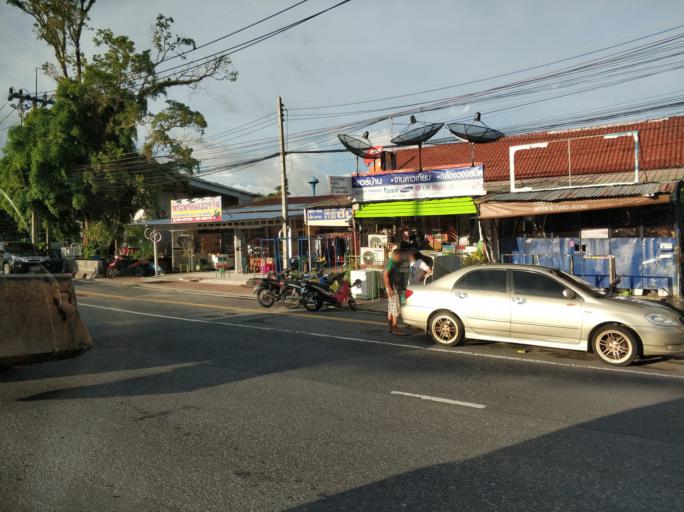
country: TH
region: Phuket
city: Kathu
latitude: 7.9030
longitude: 98.3361
